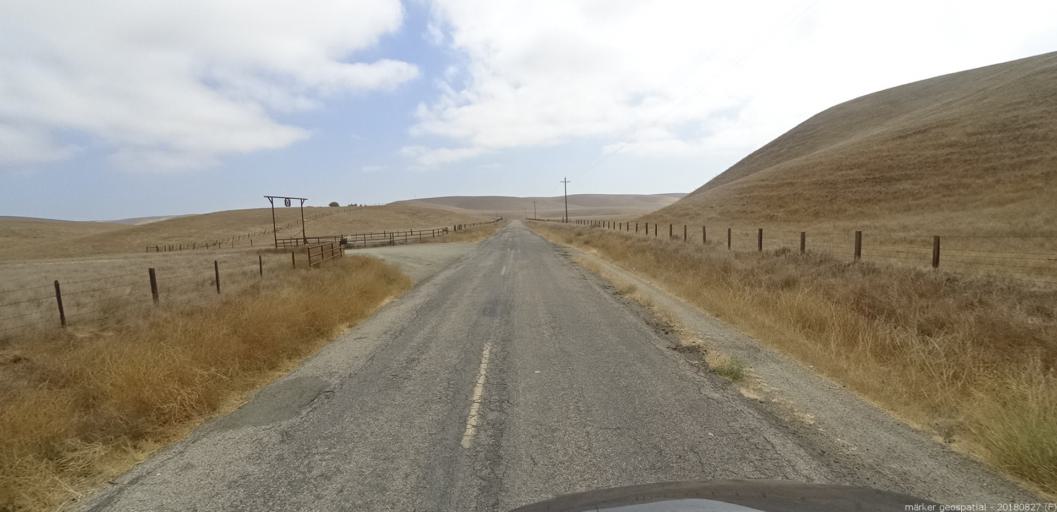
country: US
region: California
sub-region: Monterey County
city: King City
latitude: 36.2222
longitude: -121.0735
